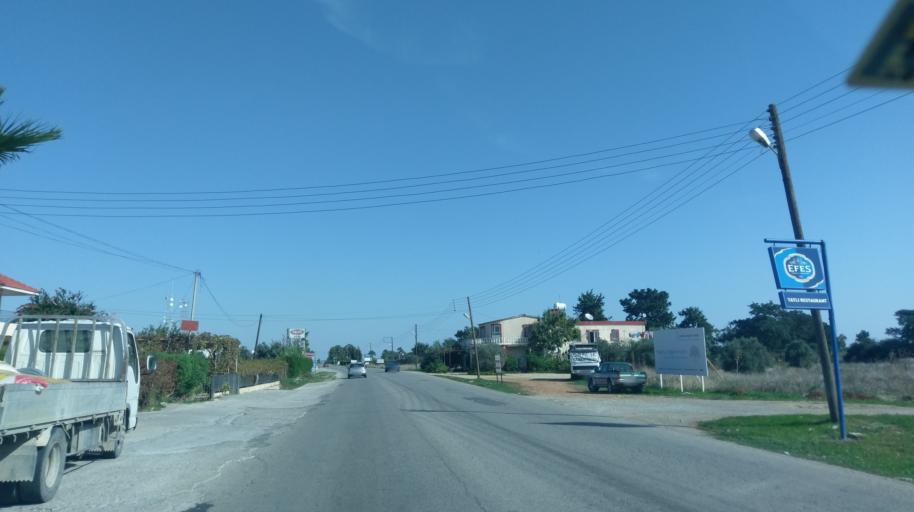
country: CY
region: Ammochostos
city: Trikomo
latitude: 35.2862
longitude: 33.9273
